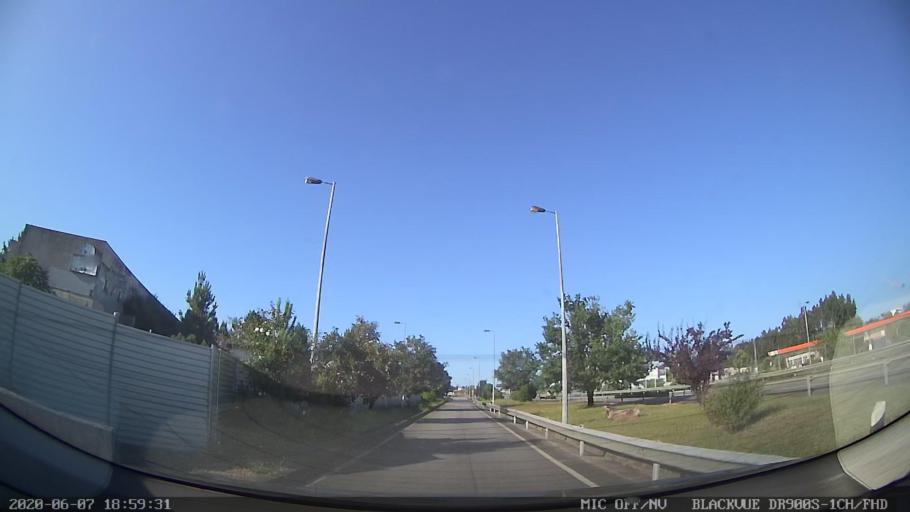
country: PT
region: Braga
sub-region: Vila Nova de Famalicao
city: Vila Nova de Famalicao
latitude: 41.3893
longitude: -8.4813
